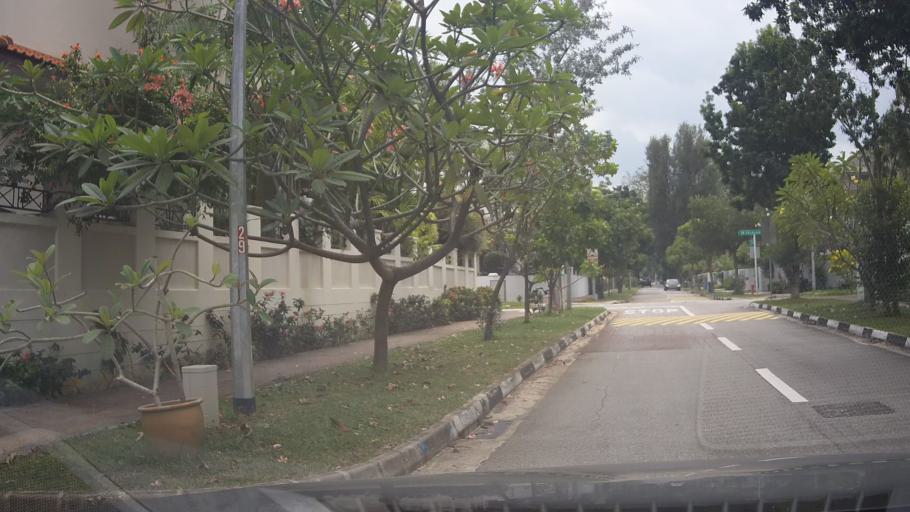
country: SG
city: Singapore
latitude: 1.3028
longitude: 103.8903
